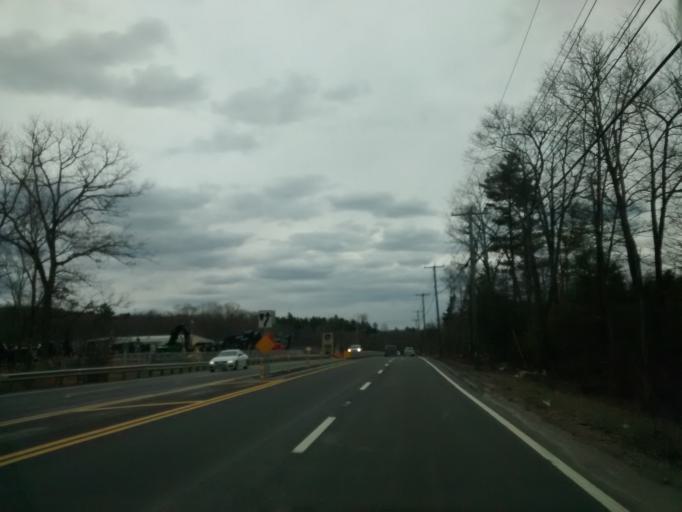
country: US
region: Massachusetts
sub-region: Worcester County
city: Oxford
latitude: 42.1620
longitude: -71.8997
